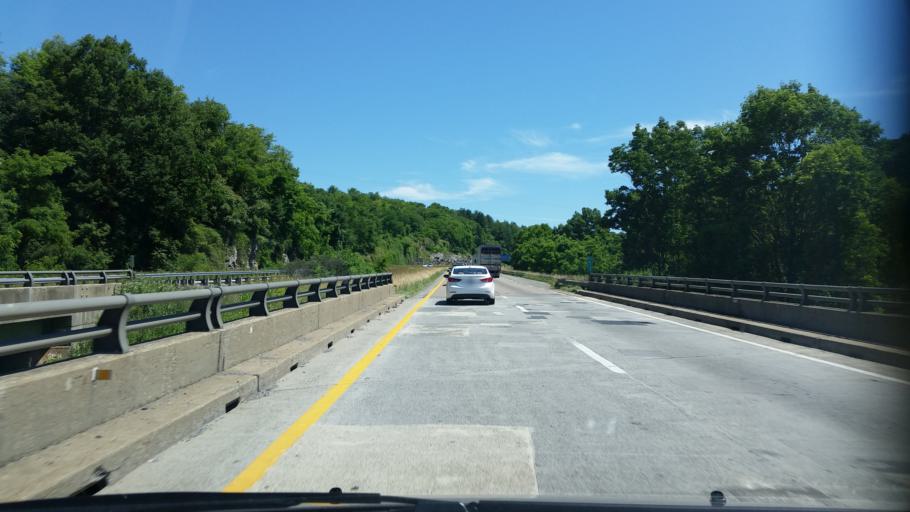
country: US
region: Virginia
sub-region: Smyth County
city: Atkins
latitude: 36.8750
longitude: -81.3983
